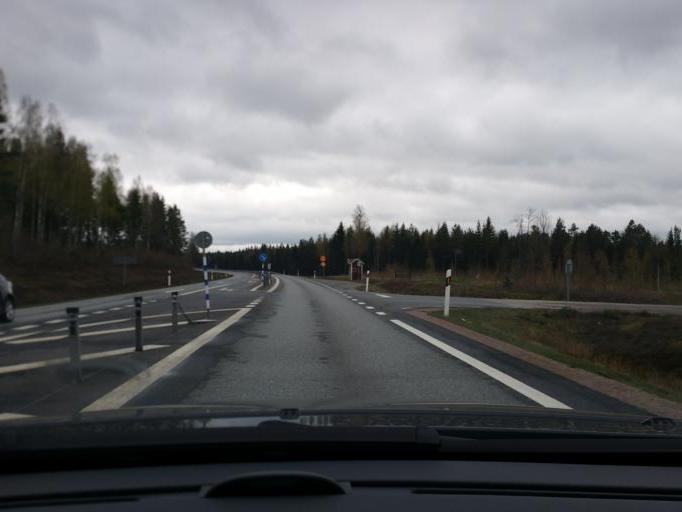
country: SE
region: Kronoberg
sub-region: Vaxjo Kommun
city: Gemla
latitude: 56.9219
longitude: 14.7170
